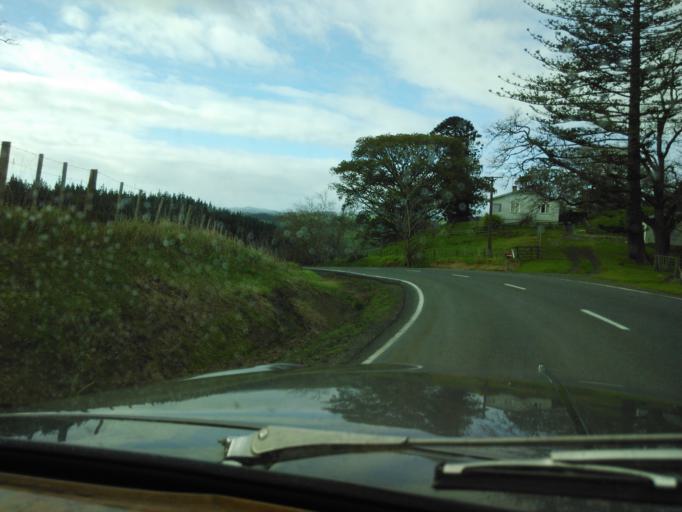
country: NZ
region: Auckland
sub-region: Auckland
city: Wellsford
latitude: -36.2834
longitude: 174.4356
